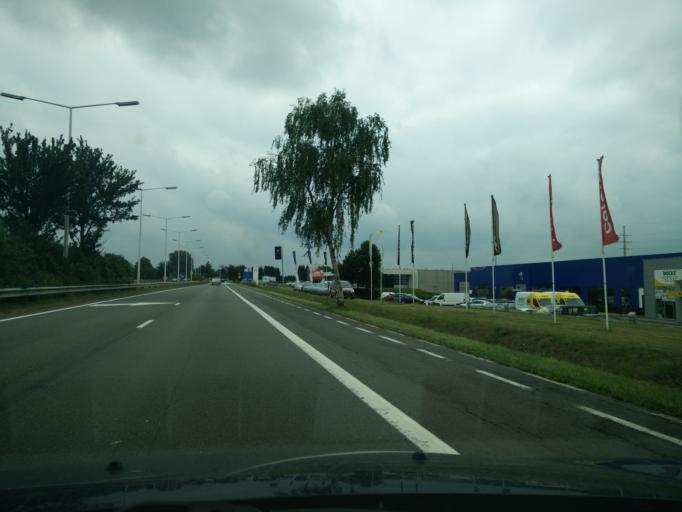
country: BE
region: Flanders
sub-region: Provincie Oost-Vlaanderen
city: Oudenaarde
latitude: 50.8646
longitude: 3.6011
